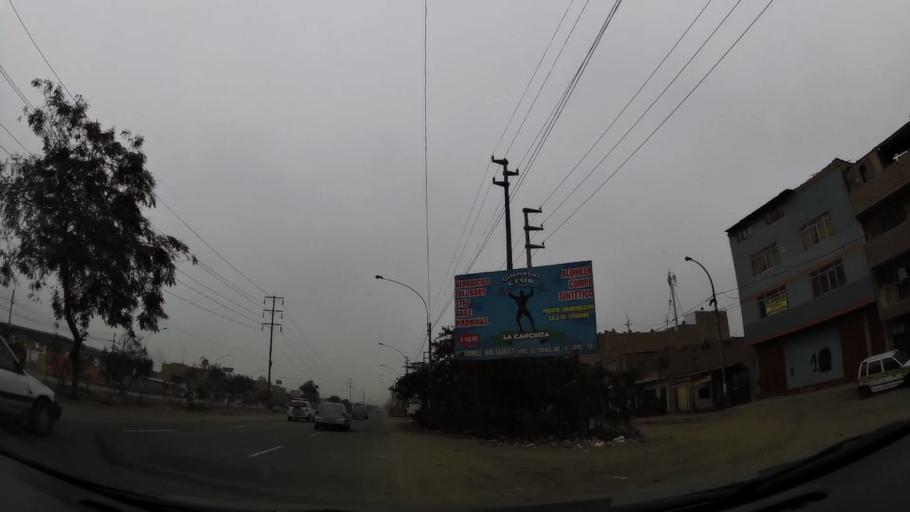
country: PE
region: Lima
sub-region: Lima
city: Urb. Santo Domingo
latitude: -11.9053
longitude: -77.0530
